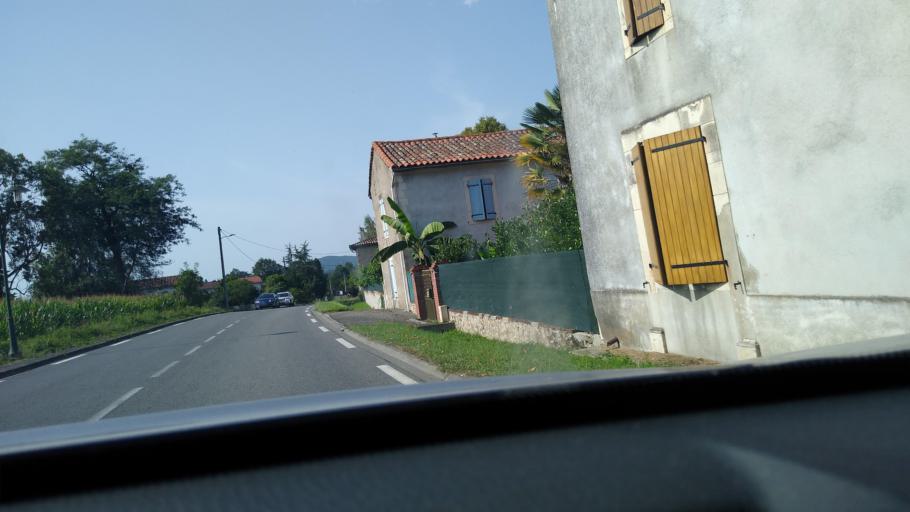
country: FR
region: Midi-Pyrenees
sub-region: Departement de la Haute-Garonne
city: Salies-du-Salat
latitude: 43.1127
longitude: 0.9369
